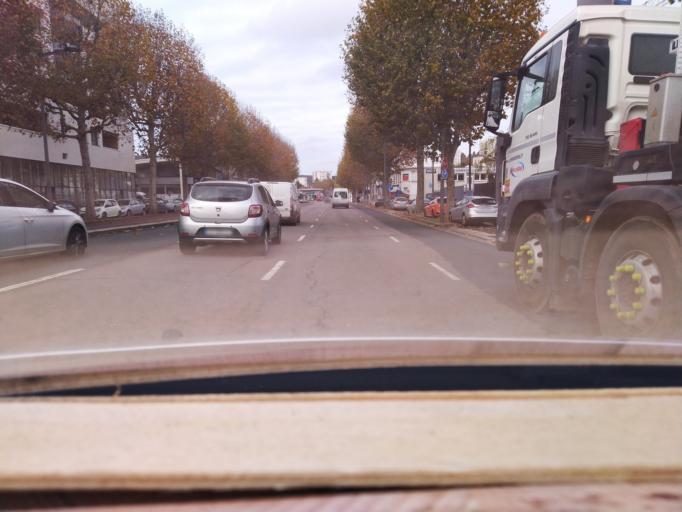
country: FR
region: Haute-Normandie
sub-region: Departement de la Seine-Maritime
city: Deville-les-Rouen
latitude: 49.4473
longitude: 1.0690
